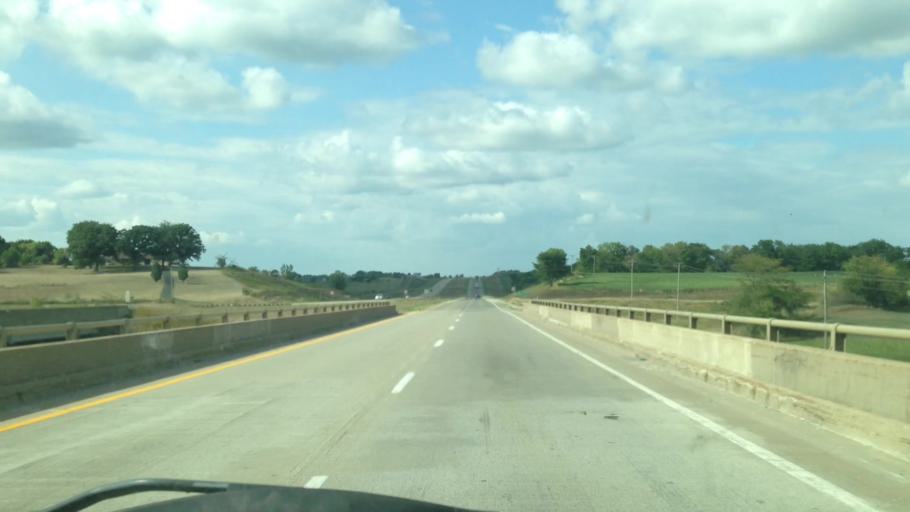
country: US
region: Iowa
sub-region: Henry County
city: Mount Pleasant
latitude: 40.8564
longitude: -91.5647
